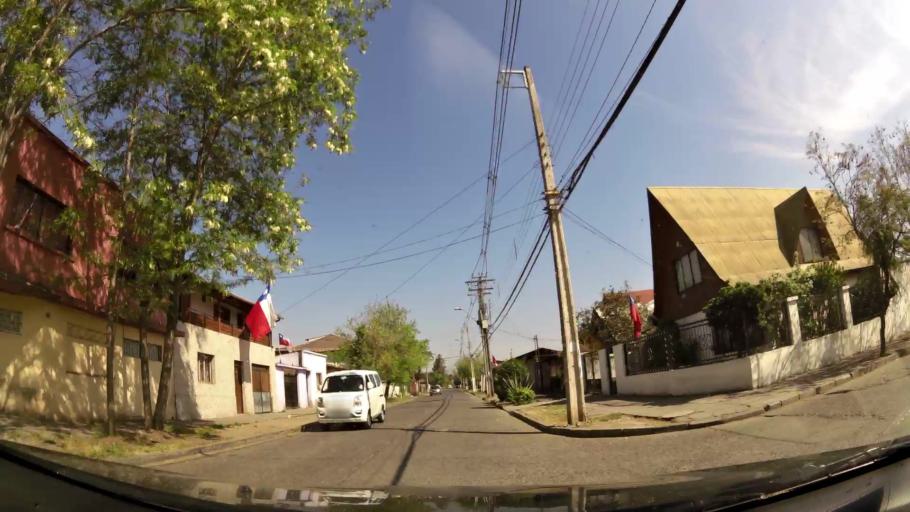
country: CL
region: Santiago Metropolitan
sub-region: Provincia de Santiago
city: Santiago
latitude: -33.3990
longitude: -70.6449
